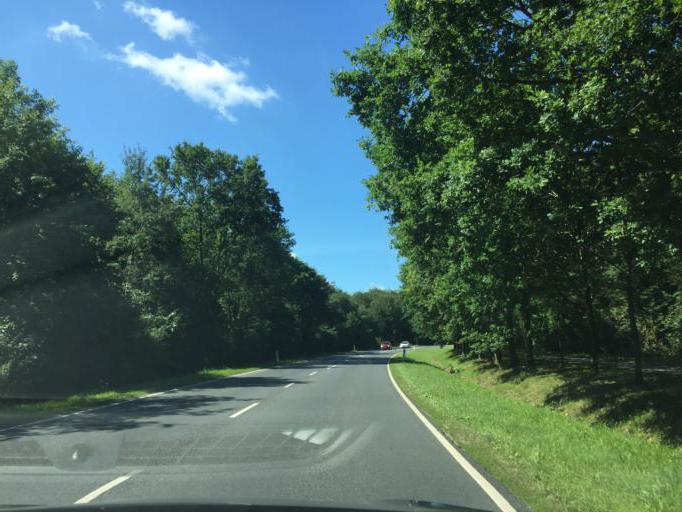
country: DK
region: South Denmark
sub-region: Odense Kommune
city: Bellinge
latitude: 55.3777
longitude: 10.3430
